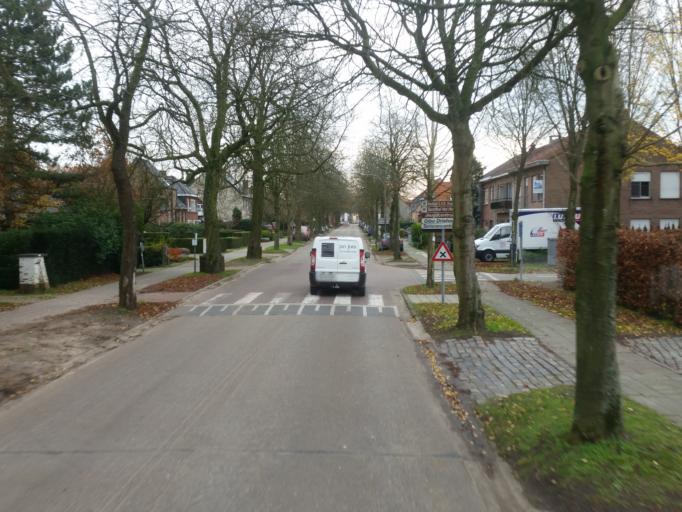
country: BE
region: Flanders
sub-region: Provincie Antwerpen
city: Brasschaat
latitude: 51.3036
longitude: 4.5123
